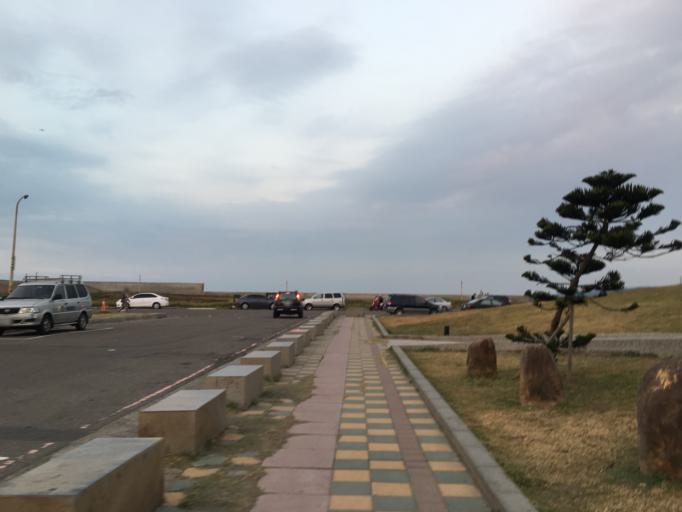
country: TW
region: Taiwan
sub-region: Hsinchu
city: Hsinchu
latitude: 24.8509
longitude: 120.9281
